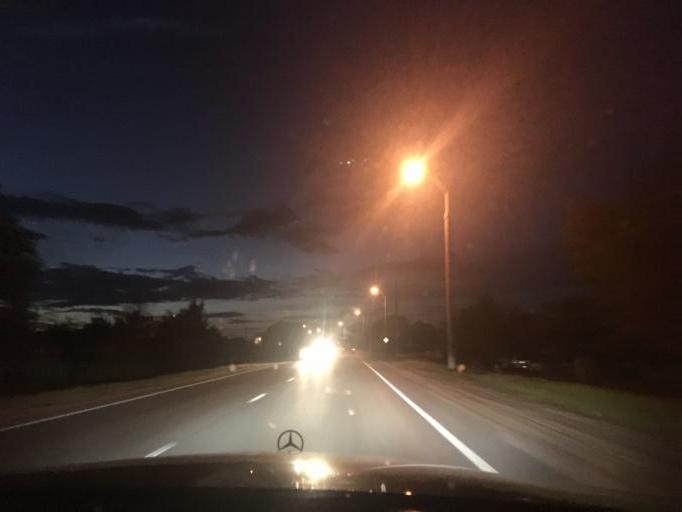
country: BY
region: Brest
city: Brest
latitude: 52.0666
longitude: 23.6853
